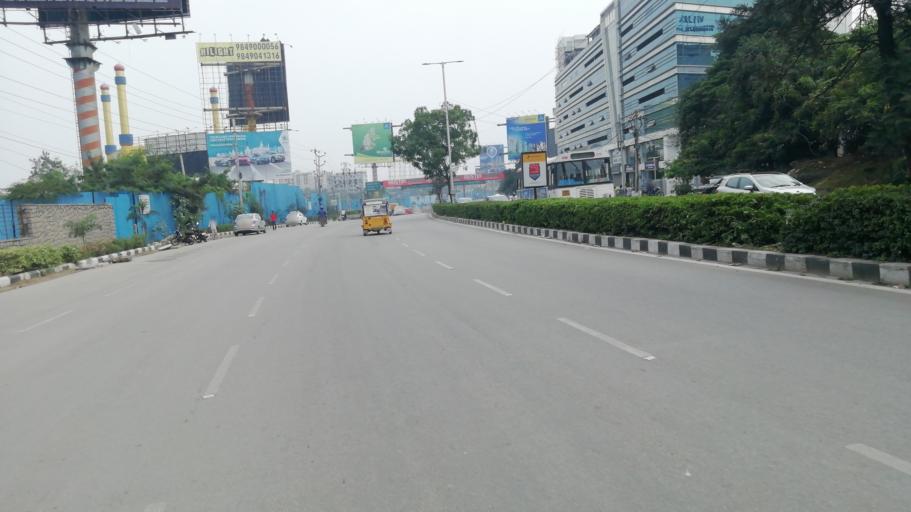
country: IN
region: Telangana
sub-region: Rangareddi
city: Kukatpalli
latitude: 17.4574
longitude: 78.3757
